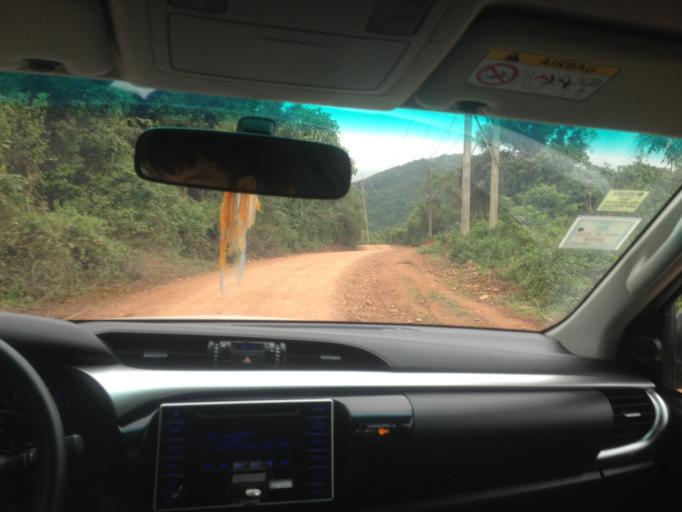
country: TH
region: Nan
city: Chaloem Phra Kiat
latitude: 19.9657
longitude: 101.1383
